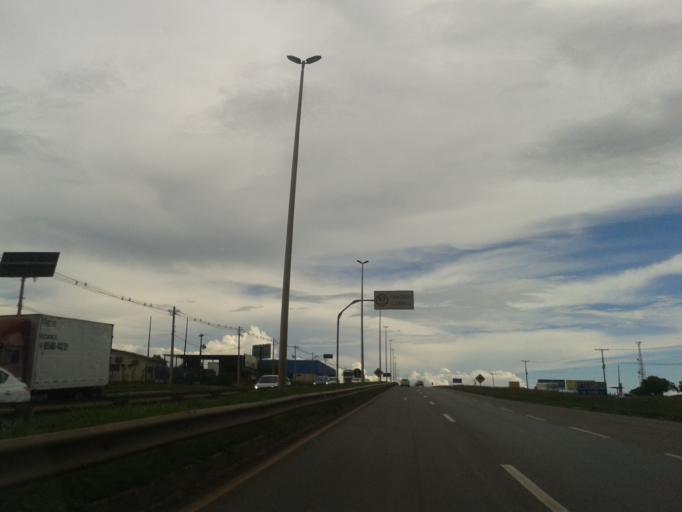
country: BR
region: Goias
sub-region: Aparecida De Goiania
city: Aparecida de Goiania
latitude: -16.7949
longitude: -49.2383
